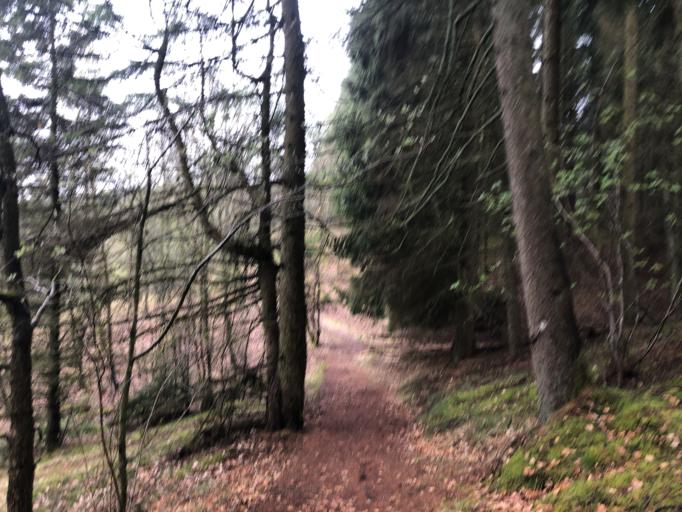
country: DK
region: Central Jutland
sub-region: Lemvig Kommune
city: Lemvig
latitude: 56.4814
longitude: 8.3550
